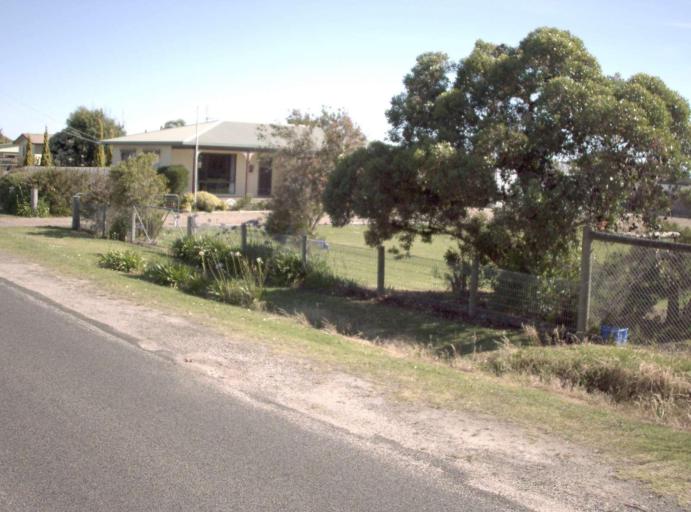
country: AU
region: Victoria
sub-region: Latrobe
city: Traralgon
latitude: -38.6665
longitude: 146.6893
